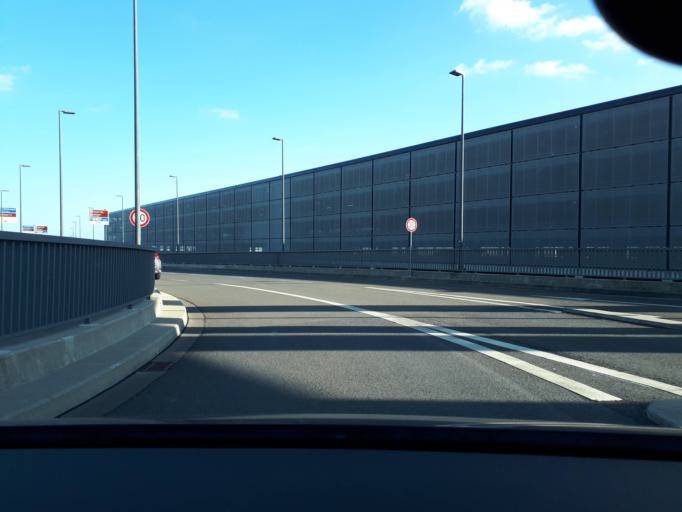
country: DE
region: Brandenburg
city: Schonefeld
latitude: 52.3623
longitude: 13.5114
